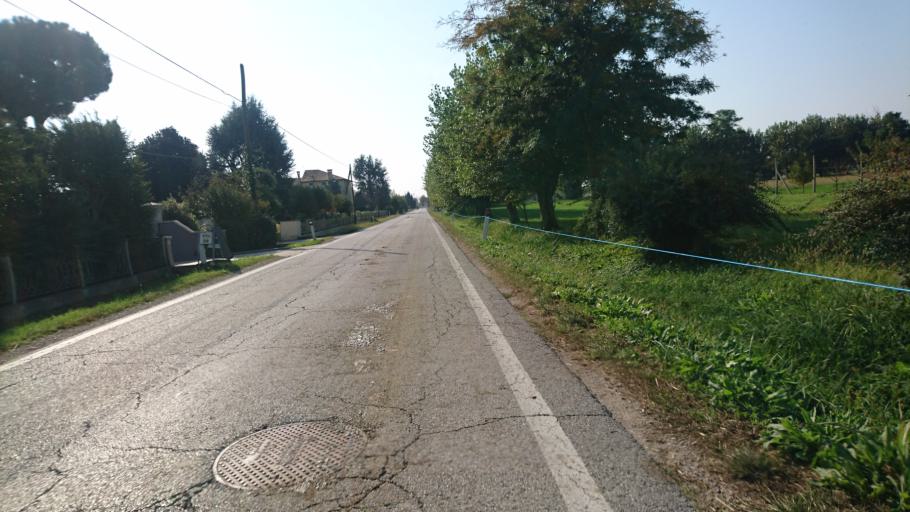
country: IT
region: Veneto
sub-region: Provincia di Padova
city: Gazzo
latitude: 45.5896
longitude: 11.7010
